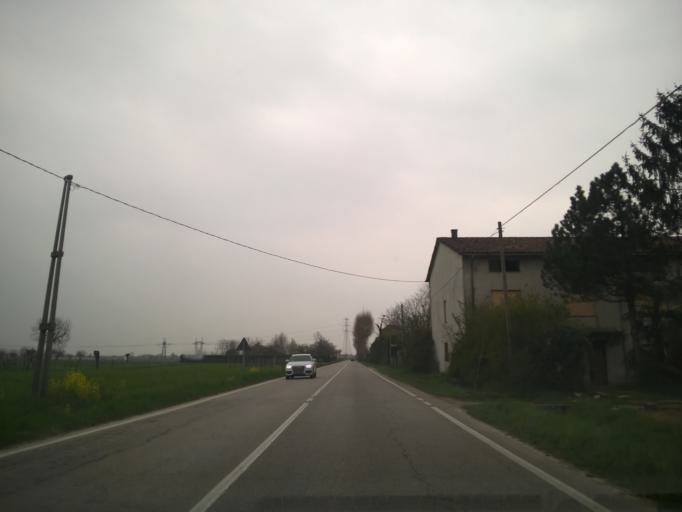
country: IT
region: Veneto
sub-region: Provincia di Vicenza
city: Montecchio Precalcino
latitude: 45.6794
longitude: 11.5699
